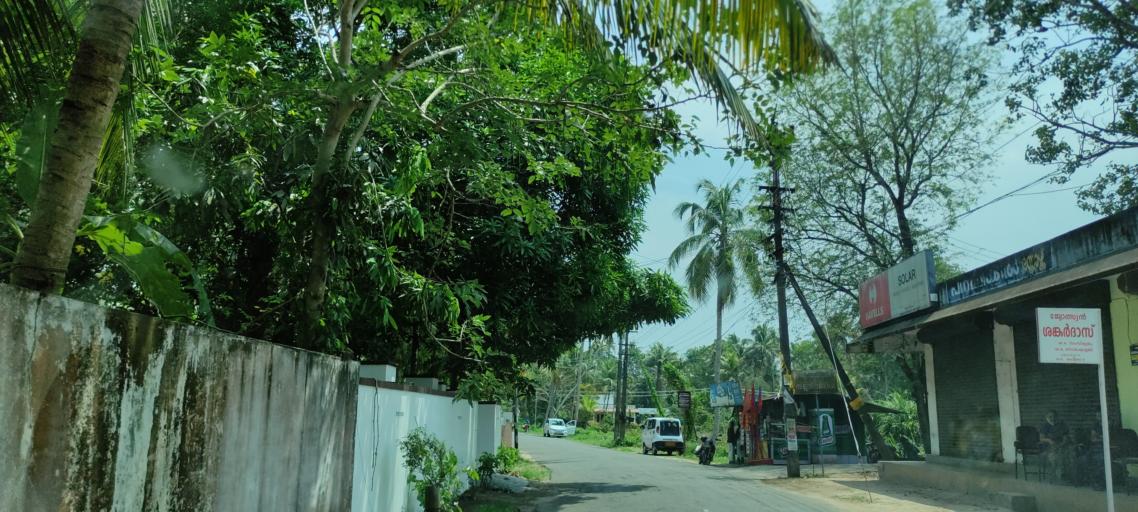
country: IN
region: Kerala
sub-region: Alappuzha
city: Vayalar
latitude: 9.7100
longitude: 76.3370
